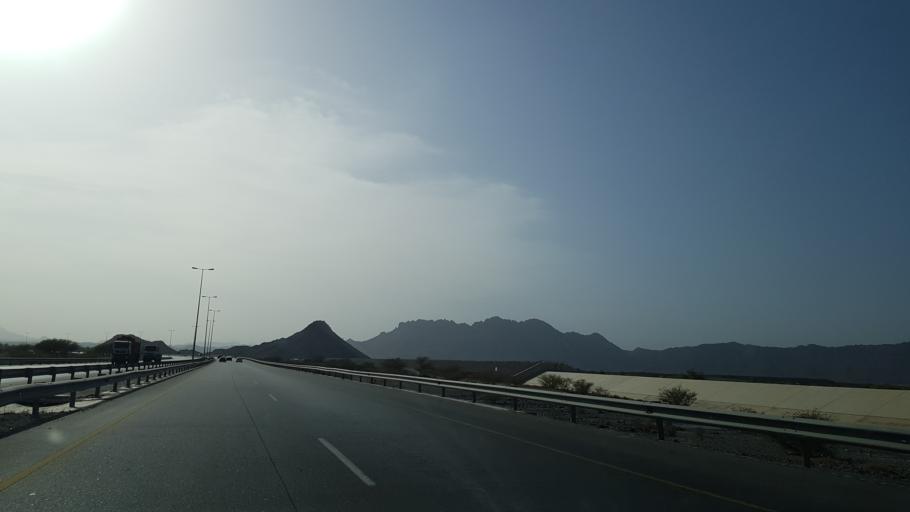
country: OM
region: Muhafazat ad Dakhiliyah
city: Nizwa
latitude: 22.8617
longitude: 57.5867
